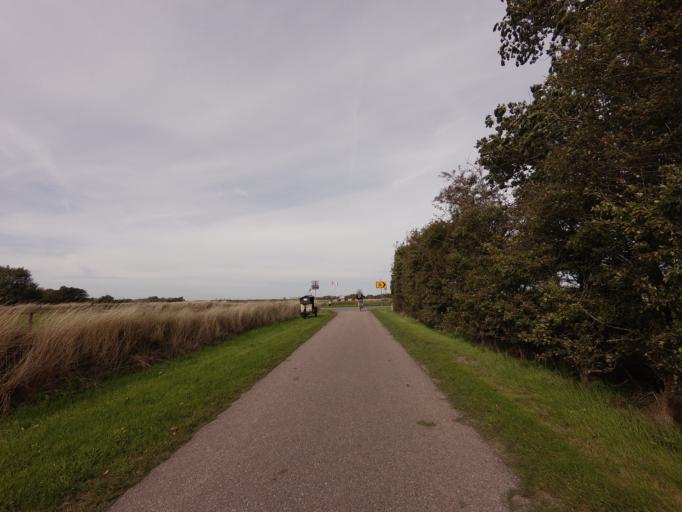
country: NL
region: North Holland
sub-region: Gemeente Texel
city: Den Burg
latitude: 53.0675
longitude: 4.8142
